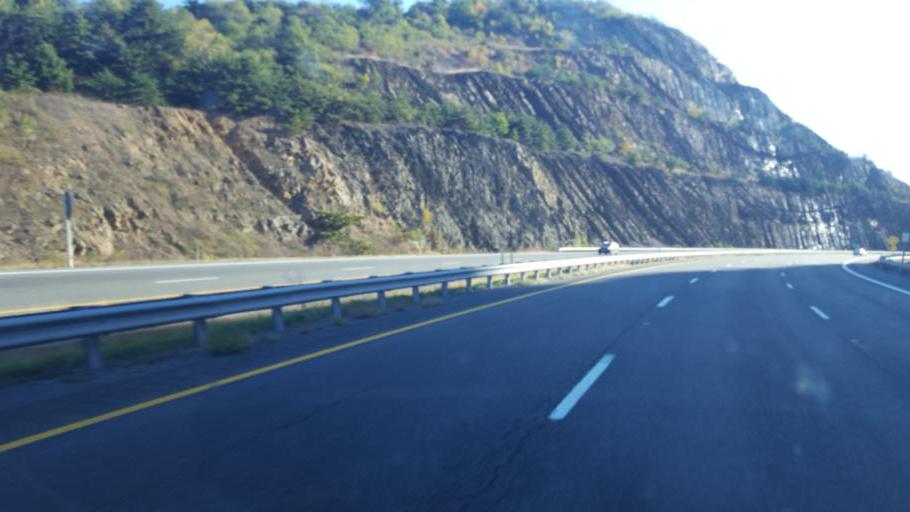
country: US
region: Maryland
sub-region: Washington County
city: Hancock
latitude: 39.7195
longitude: -78.2865
